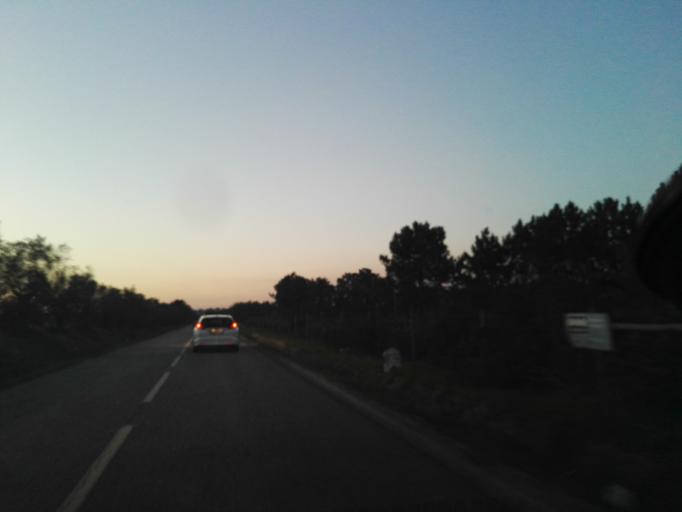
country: PT
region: Setubal
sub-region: Alcochete
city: Alcochete
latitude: 38.7292
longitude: -8.9190
